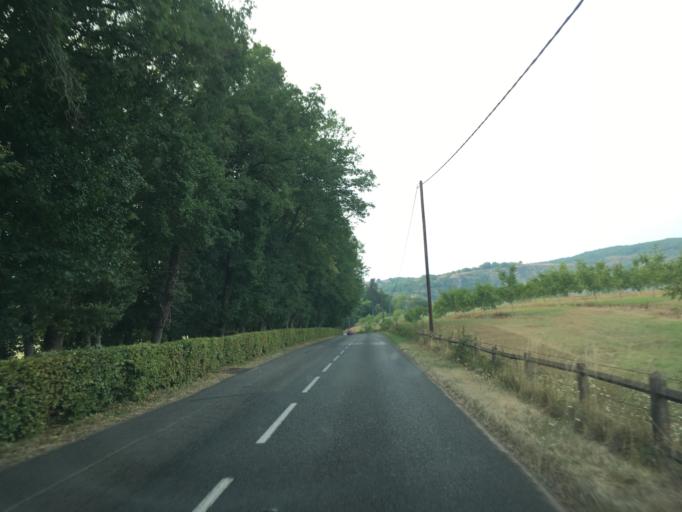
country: FR
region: Midi-Pyrenees
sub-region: Departement du Lot
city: Souillac
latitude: 44.8491
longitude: 1.5309
